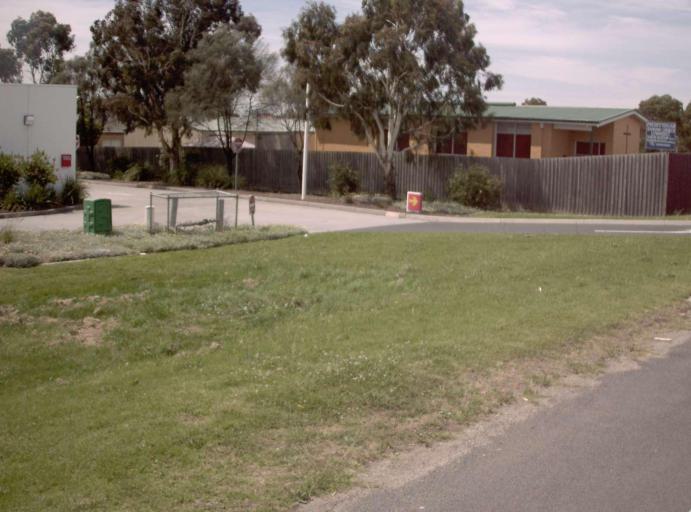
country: AU
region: Victoria
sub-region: Casey
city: Lynbrook
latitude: -38.0553
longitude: 145.2440
